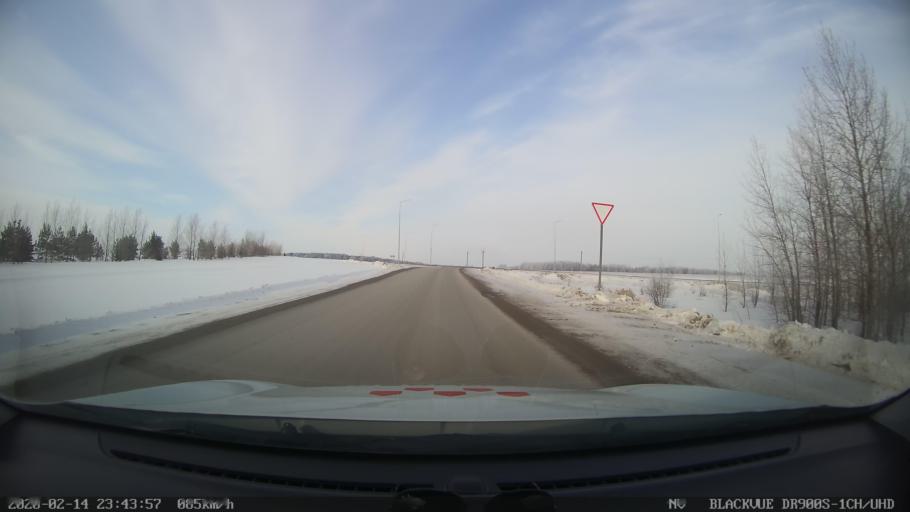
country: RU
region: Tatarstan
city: Kuybyshevskiy Zaton
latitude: 55.2082
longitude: 49.2473
